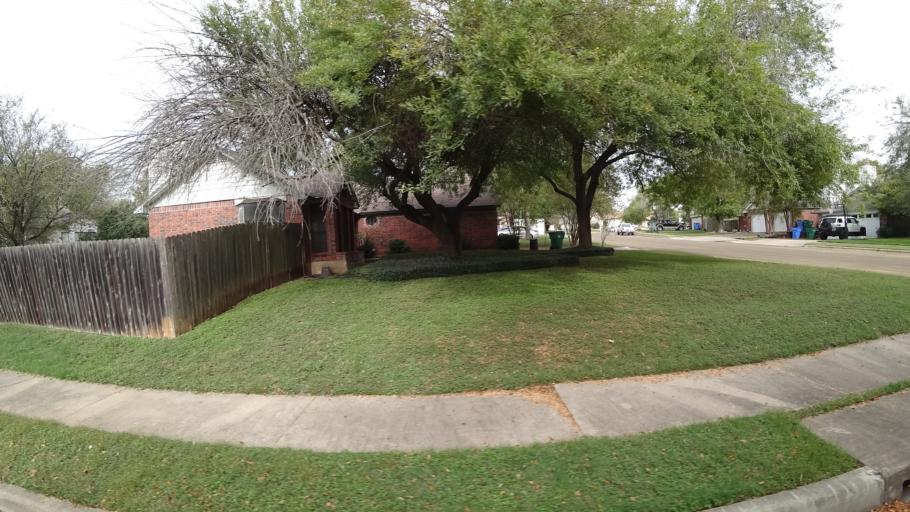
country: US
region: Texas
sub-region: Travis County
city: Wells Branch
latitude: 30.4433
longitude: -97.6779
